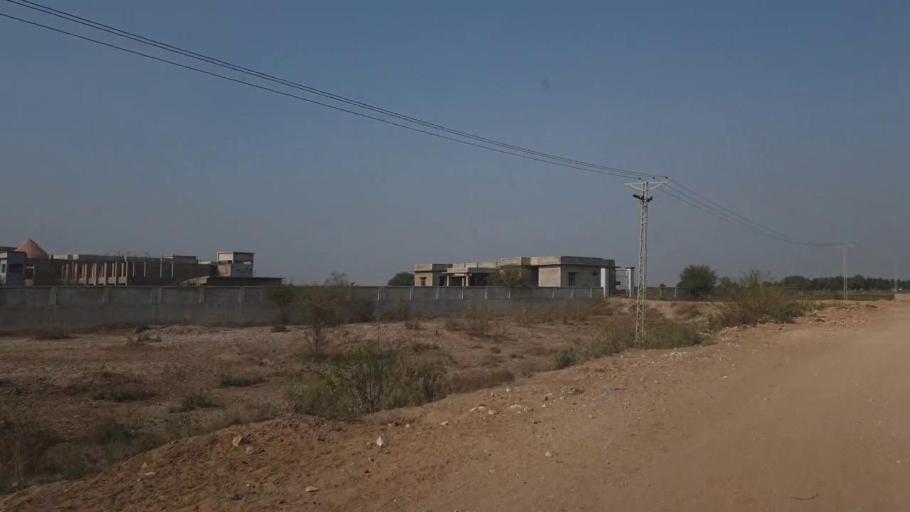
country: PK
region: Sindh
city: Tando Allahyar
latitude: 25.4354
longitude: 68.7042
